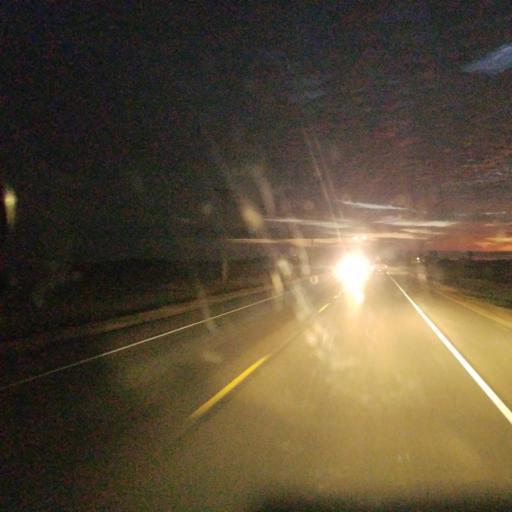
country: US
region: Illinois
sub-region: Peoria County
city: Hanna City
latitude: 40.6973
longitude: -89.8445
